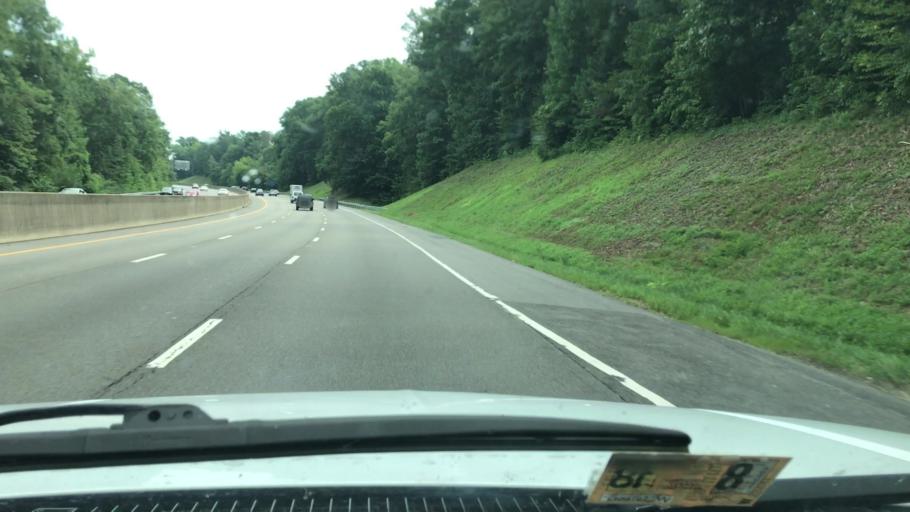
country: US
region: Virginia
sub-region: Chesterfield County
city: Bensley
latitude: 37.4562
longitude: -77.4947
